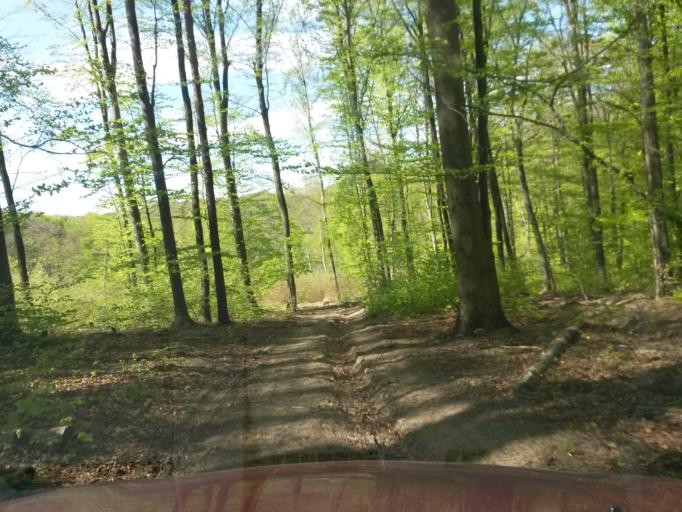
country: SK
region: Presovsky
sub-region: Okres Presov
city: Presov
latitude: 48.9428
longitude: 21.1356
